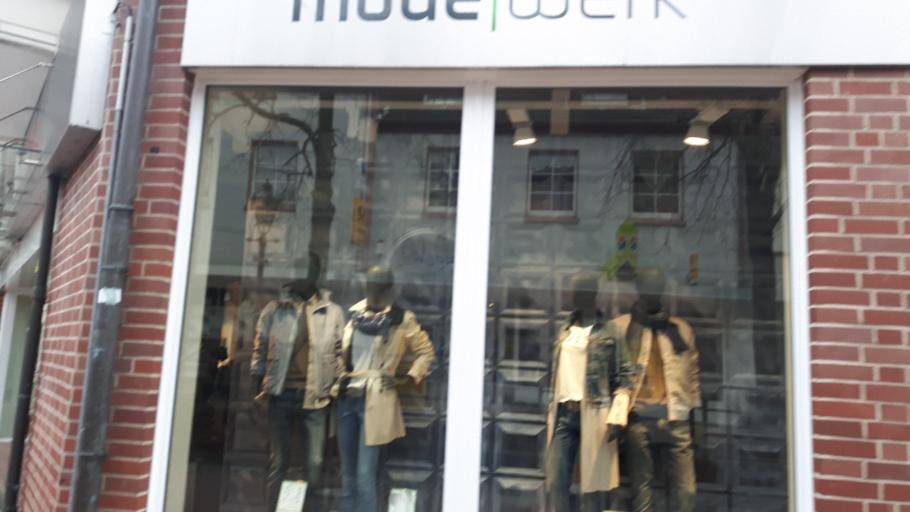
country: DE
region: North Rhine-Westphalia
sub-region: Regierungsbezirk Munster
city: Haltern
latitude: 51.7448
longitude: 7.1832
